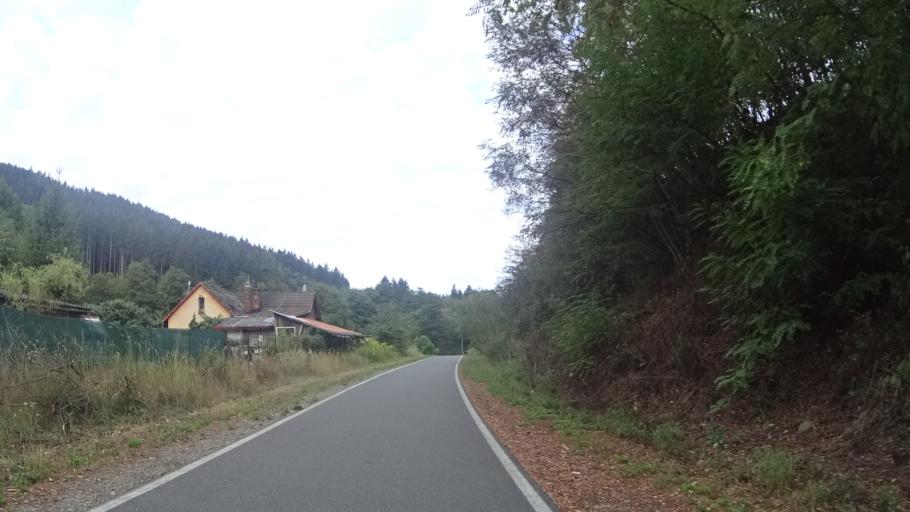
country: CZ
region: Olomoucky
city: Zabreh
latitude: 49.8634
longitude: 16.8119
